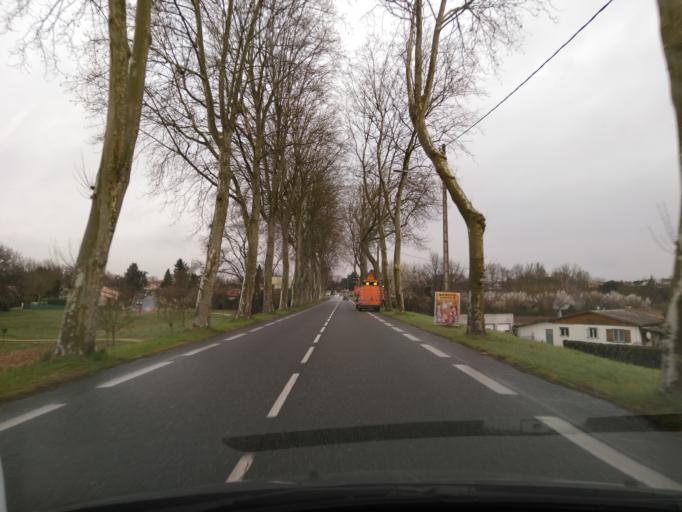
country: FR
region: Midi-Pyrenees
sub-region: Departement de la Haute-Garonne
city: Carbonne
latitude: 43.2918
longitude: 1.2164
